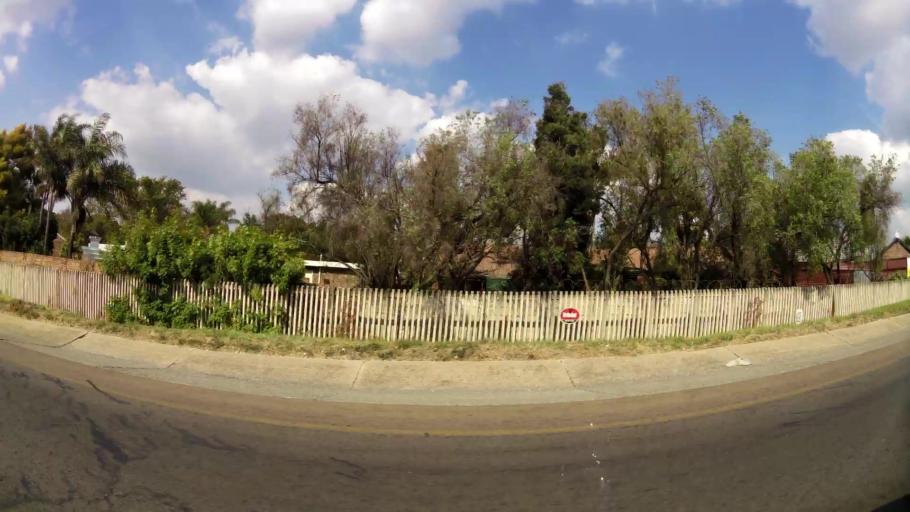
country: ZA
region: Gauteng
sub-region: City of Tshwane Metropolitan Municipality
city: Centurion
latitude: -25.8077
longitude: 28.2898
